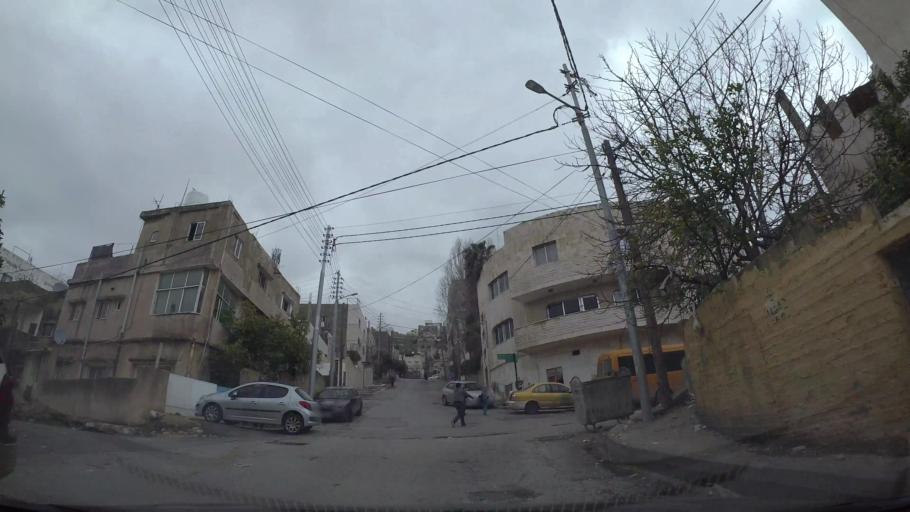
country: JO
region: Amman
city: Wadi as Sir
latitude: 31.9515
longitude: 35.8224
